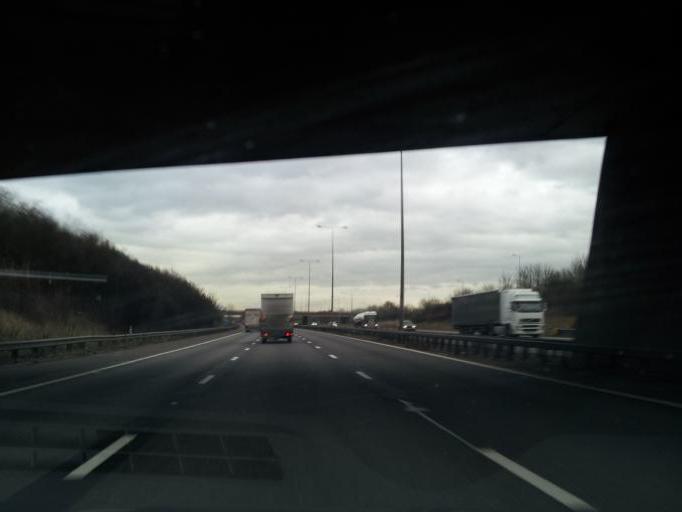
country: GB
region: England
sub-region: Warwickshire
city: Bedworth
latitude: 52.4378
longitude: -1.4286
